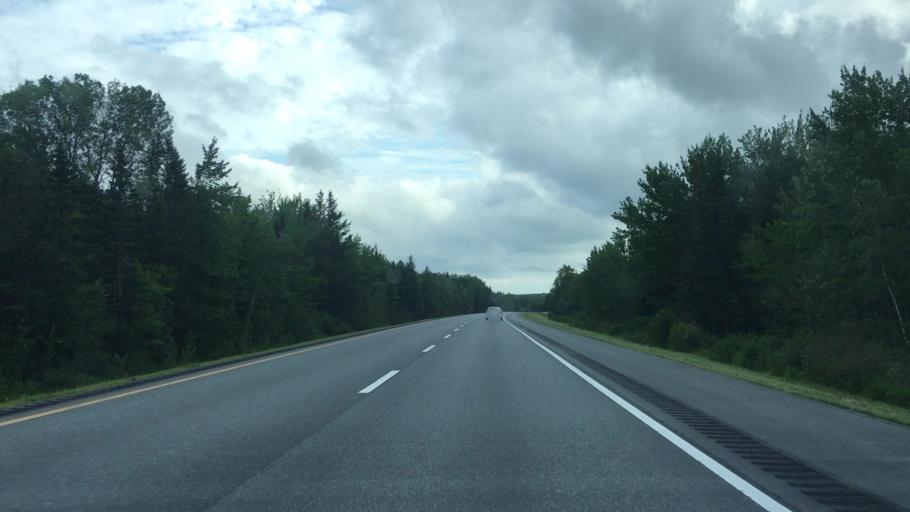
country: US
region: Maine
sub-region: Waldo County
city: Burnham
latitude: 44.7155
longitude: -69.4472
